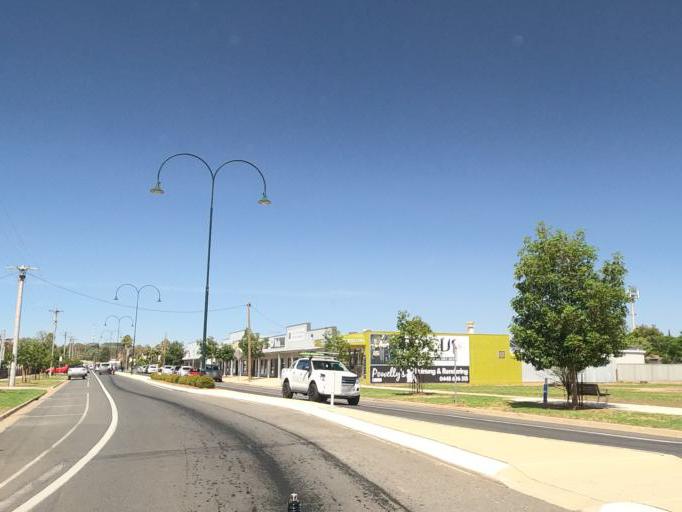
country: AU
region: New South Wales
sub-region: Corowa Shire
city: Mulwala
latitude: -35.9896
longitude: 146.0052
